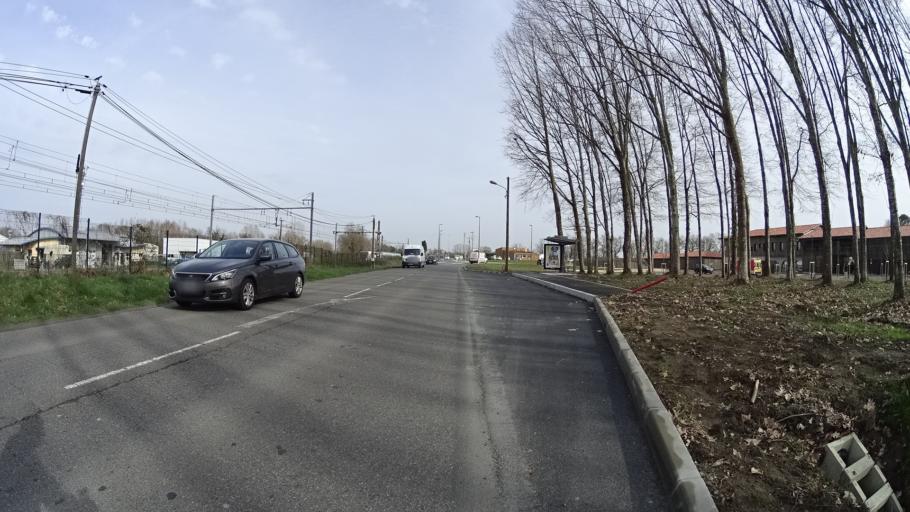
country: FR
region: Aquitaine
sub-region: Departement des Landes
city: Dax
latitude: 43.6943
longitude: -1.0340
